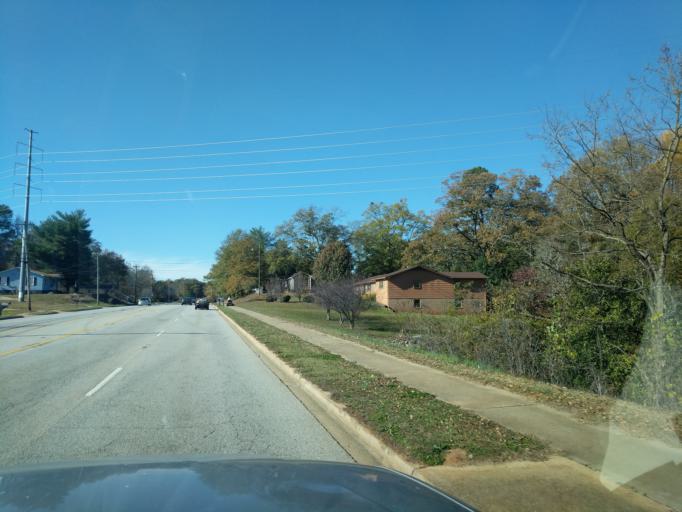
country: US
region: South Carolina
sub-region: Greenville County
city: Greer
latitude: 34.9234
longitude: -82.2176
